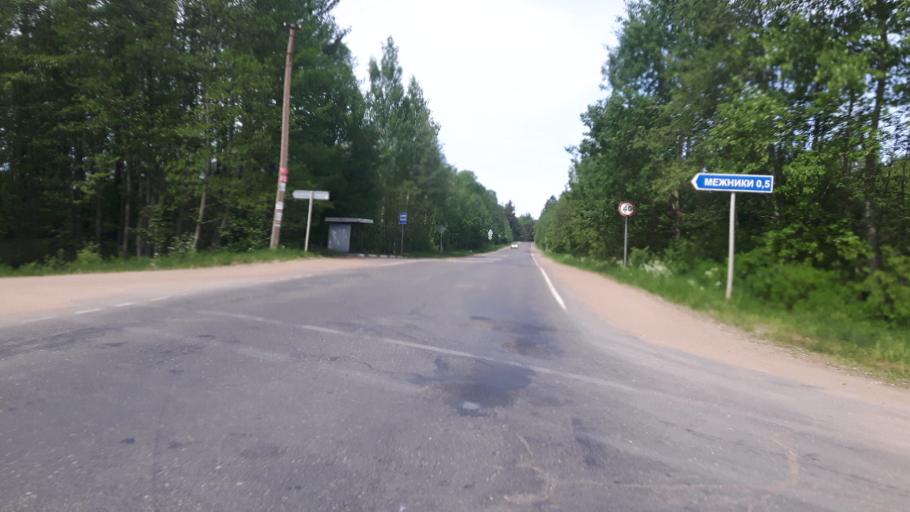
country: RU
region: Leningrad
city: Ust'-Luga
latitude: 59.6457
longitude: 28.2682
